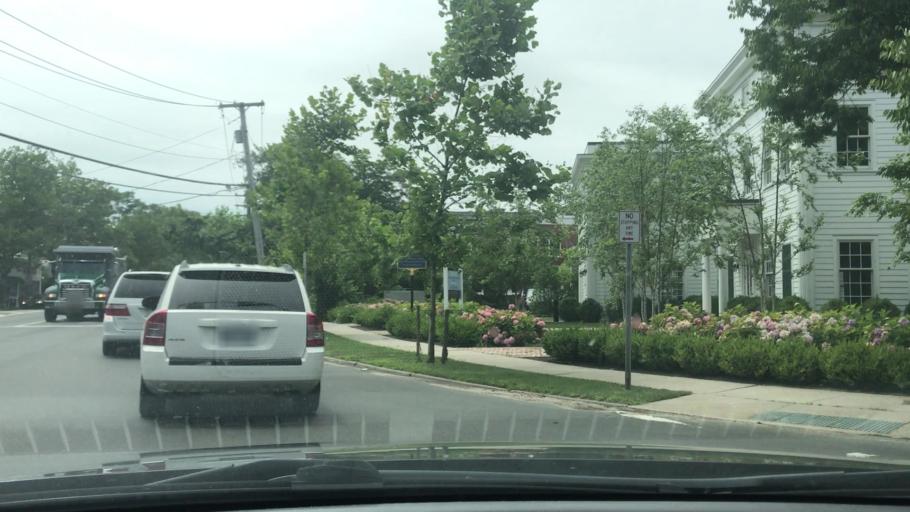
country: US
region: New York
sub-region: Suffolk County
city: Bridgehampton
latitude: 40.9378
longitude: -72.3007
